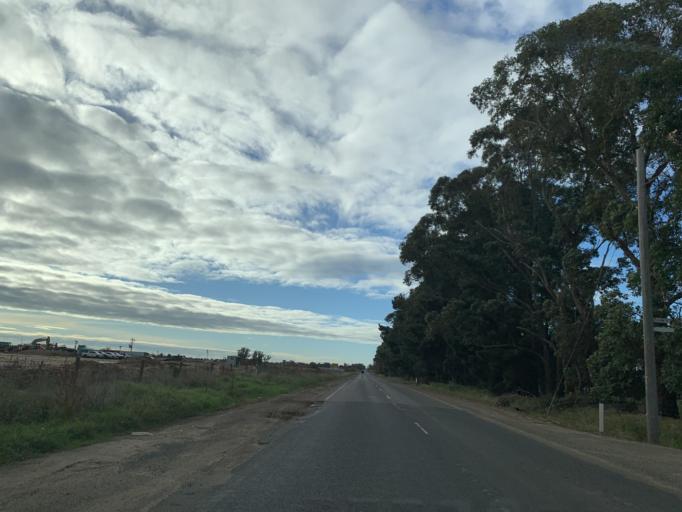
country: AU
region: Victoria
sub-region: Cardinia
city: Officer South
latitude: -38.1390
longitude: 145.3684
